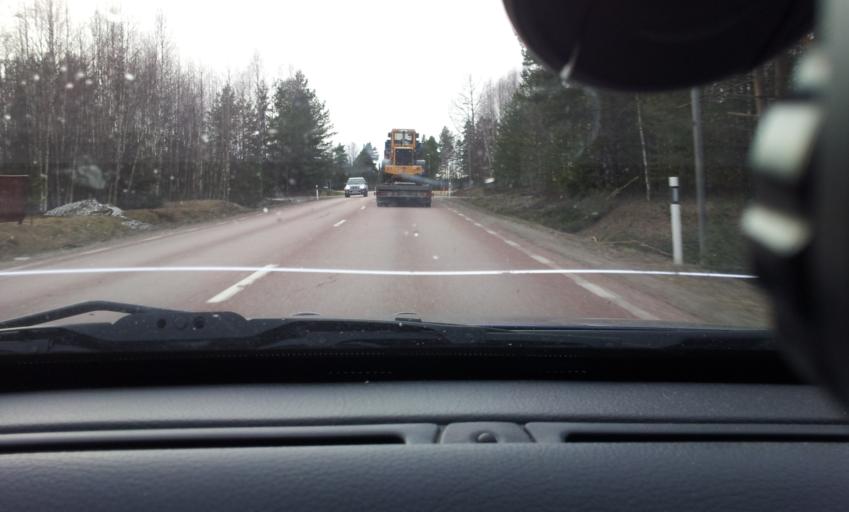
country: SE
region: Gaevleborg
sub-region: Ljusdals Kommun
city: Farila
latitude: 61.8009
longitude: 15.7968
